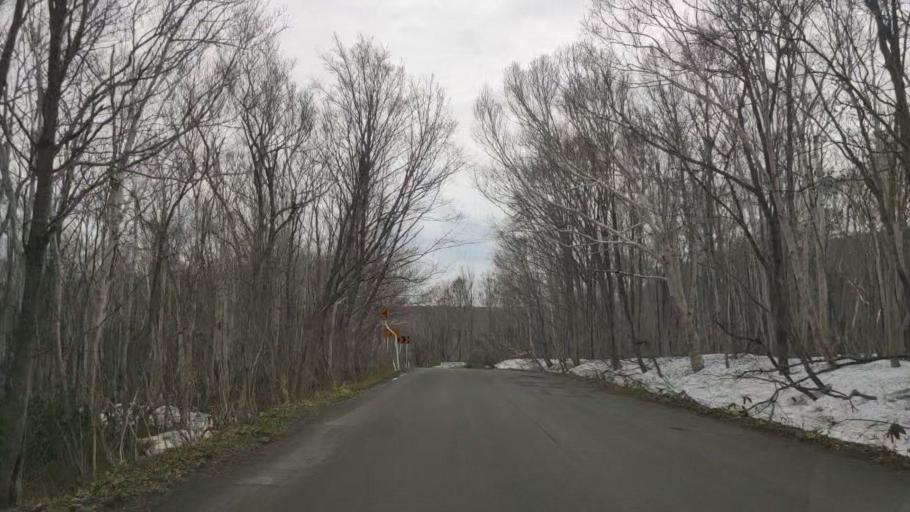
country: JP
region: Aomori
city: Aomori Shi
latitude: 40.6960
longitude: 140.9080
